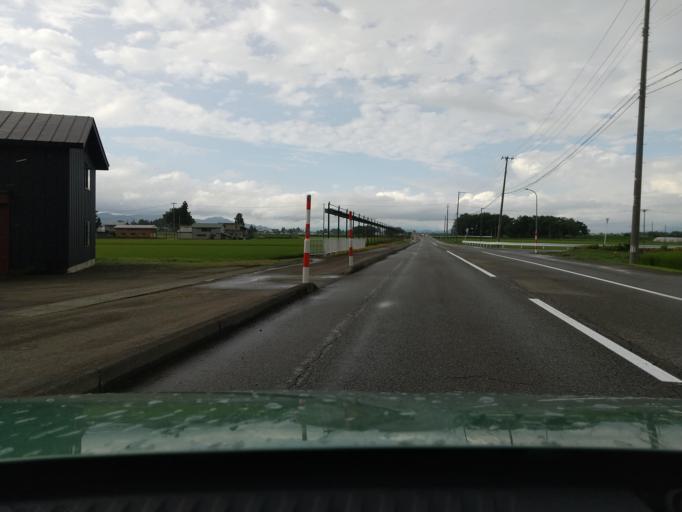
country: JP
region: Akita
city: Omagari
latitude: 39.3727
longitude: 140.4718
